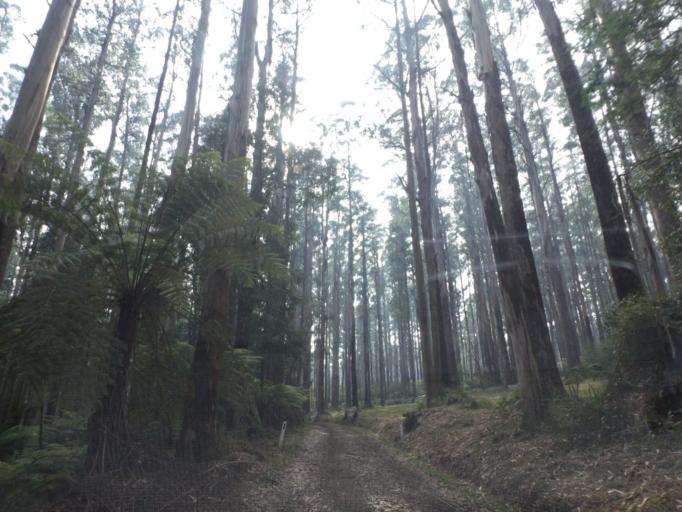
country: AU
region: Victoria
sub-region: Yarra Ranges
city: Healesville
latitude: -37.5688
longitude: 145.5838
